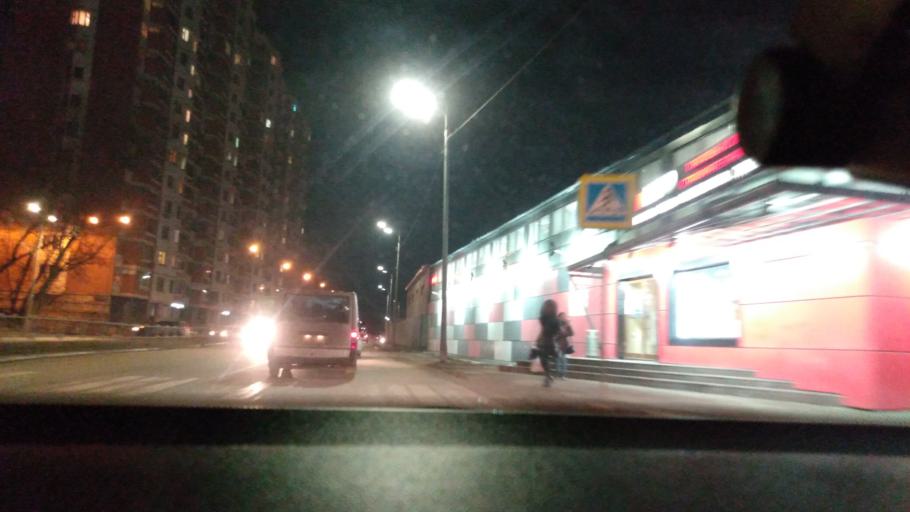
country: RU
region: Moskovskaya
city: Balashikha
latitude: 55.8182
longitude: 37.9529
